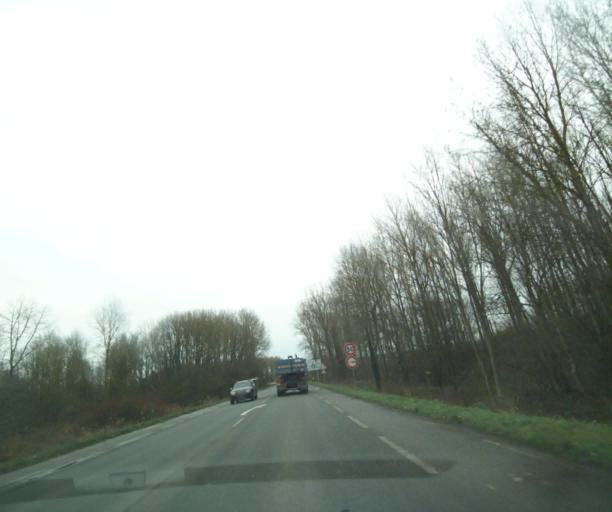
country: FR
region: Nord-Pas-de-Calais
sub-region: Departement du Nord
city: Vicq
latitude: 50.4101
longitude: 3.5819
